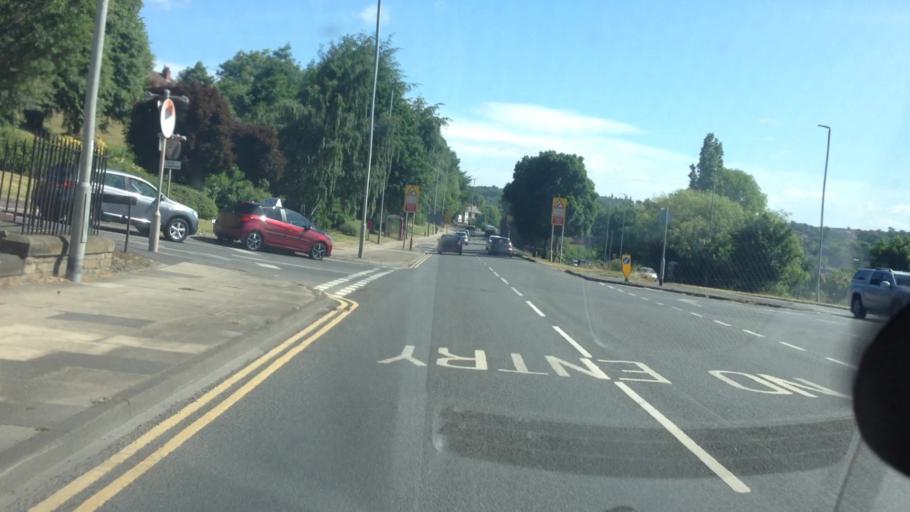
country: GB
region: England
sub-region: Kirklees
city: Dewsbury
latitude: 53.6875
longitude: -1.6410
